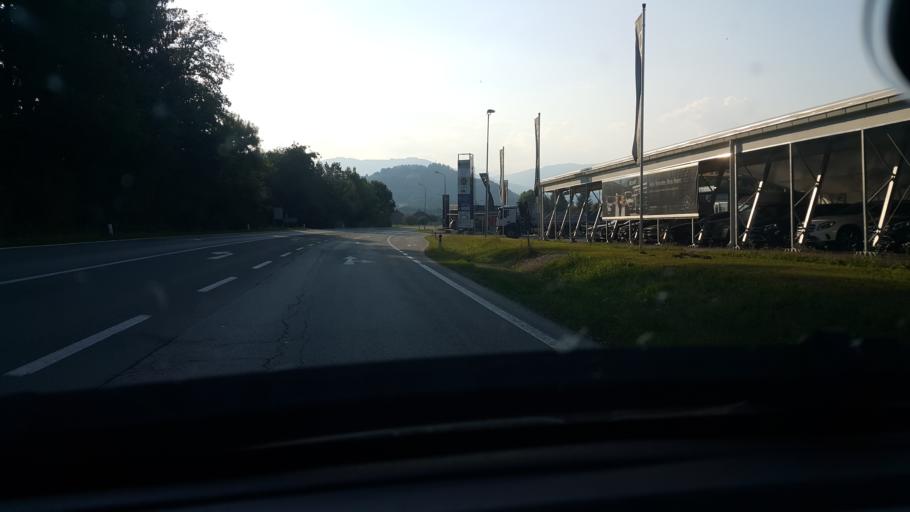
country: AT
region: Carinthia
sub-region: Politischer Bezirk Feldkirchen
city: Feldkirchen in Karnten
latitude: 46.6927
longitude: 14.1279
